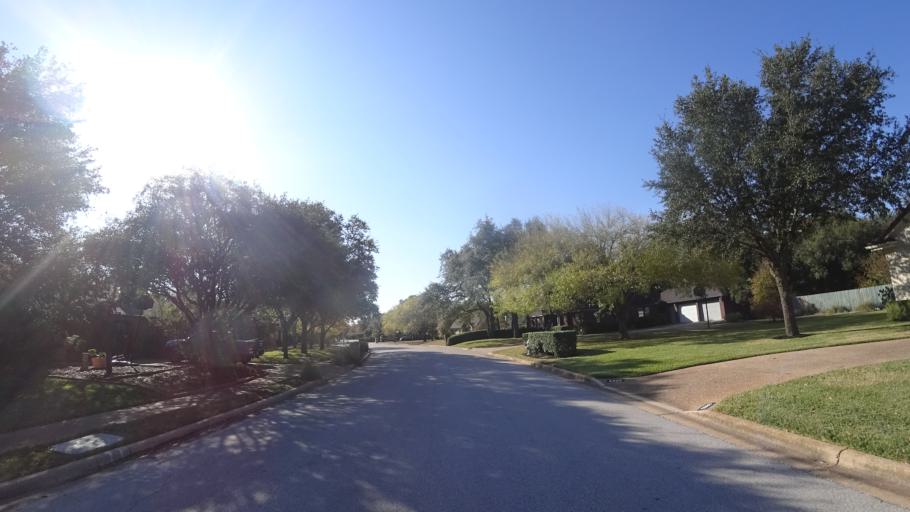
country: US
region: Texas
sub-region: Travis County
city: Shady Hollow
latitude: 30.2231
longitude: -97.8488
